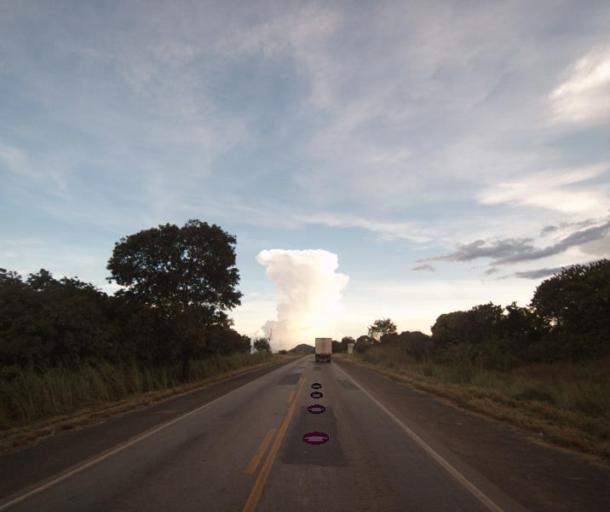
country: BR
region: Goias
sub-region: Uruacu
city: Uruacu
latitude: -14.3316
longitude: -49.1539
